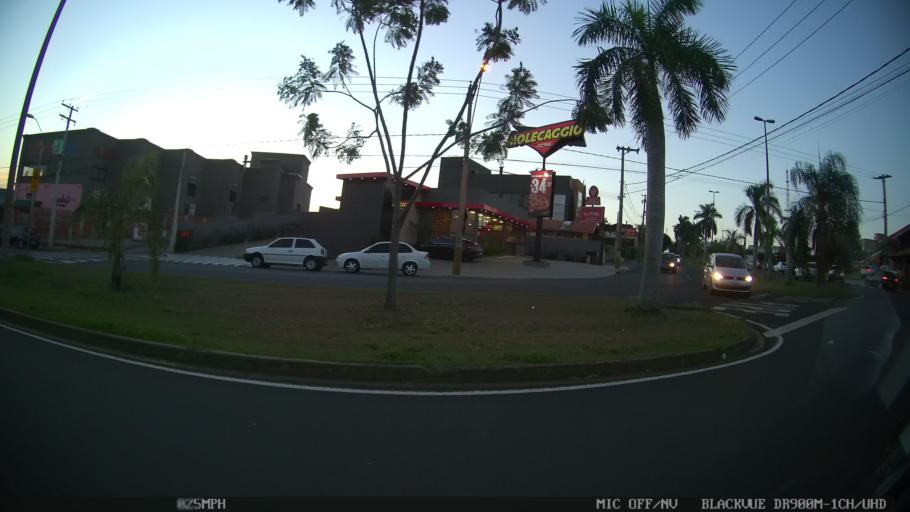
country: BR
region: Sao Paulo
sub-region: Sao Jose Do Rio Preto
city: Sao Jose do Rio Preto
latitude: -20.8071
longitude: -49.3481
